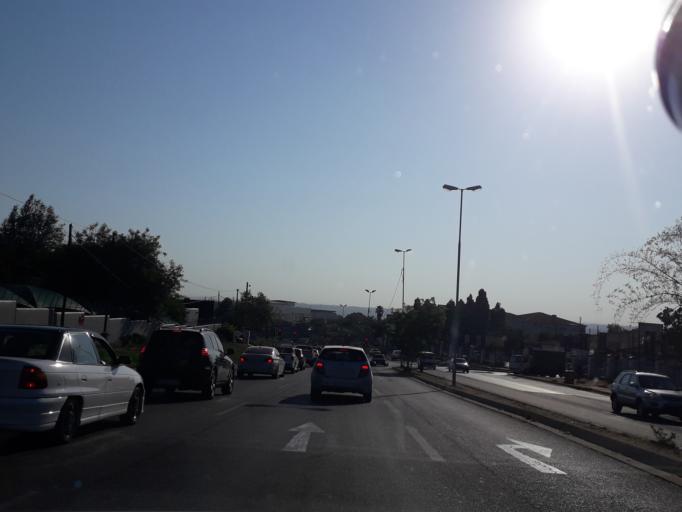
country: ZA
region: Gauteng
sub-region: West Rand District Municipality
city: Muldersdriseloop
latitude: -26.0619
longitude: 27.9527
